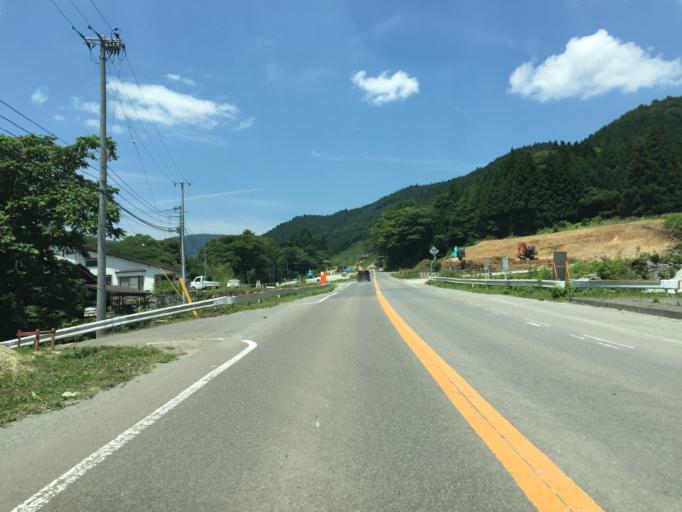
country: JP
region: Miyagi
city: Marumori
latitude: 37.7694
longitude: 140.8453
